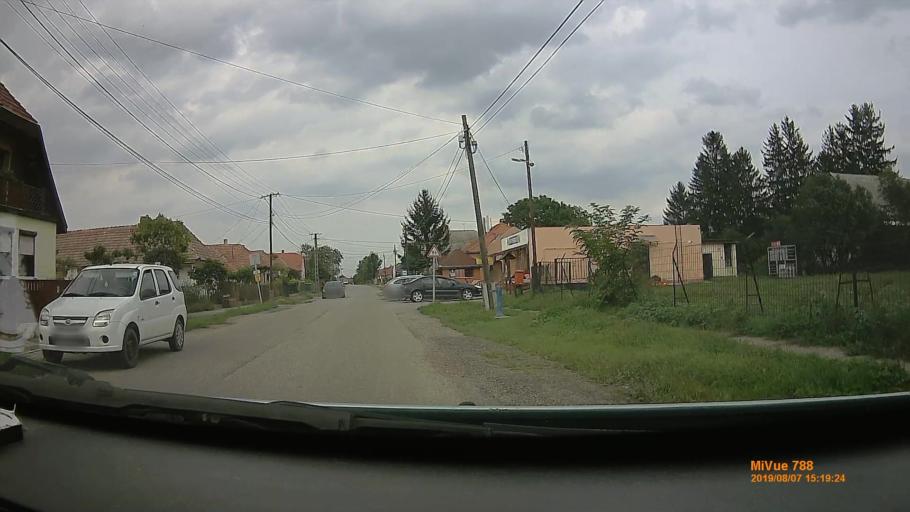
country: HU
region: Borsod-Abauj-Zemplen
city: Encs
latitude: 48.3498
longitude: 21.1426
